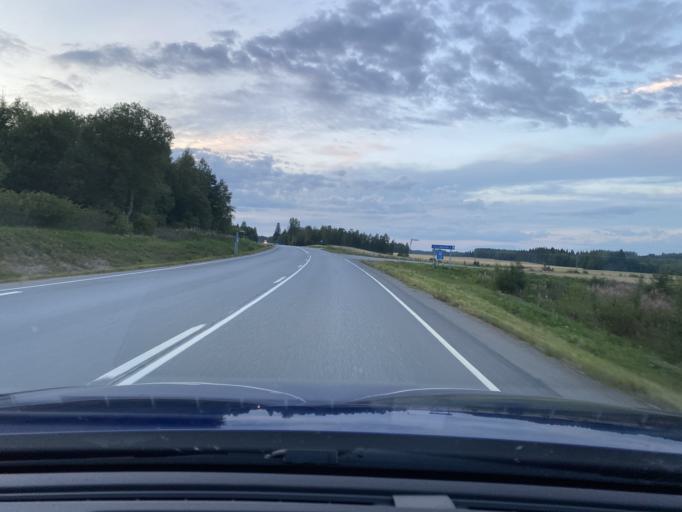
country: FI
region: Satakunta
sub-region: Pohjois-Satakunta
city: Honkajoki
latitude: 62.0996
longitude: 22.2444
